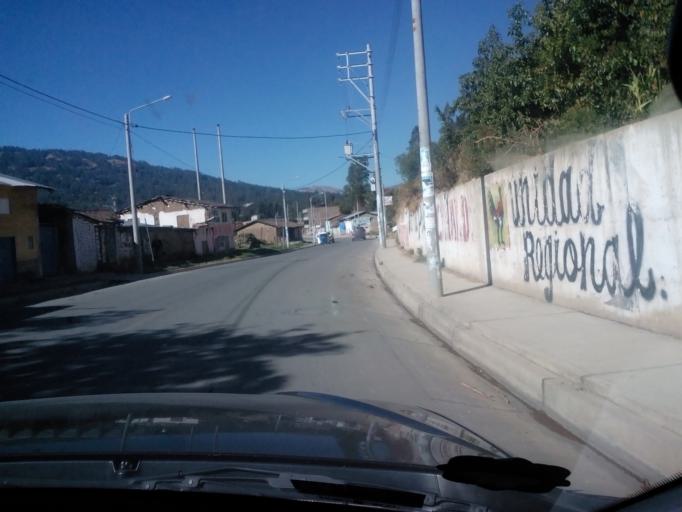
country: PE
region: Apurimac
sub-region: Provincia de Andahuaylas
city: Talavera
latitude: -13.6589
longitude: -73.4358
